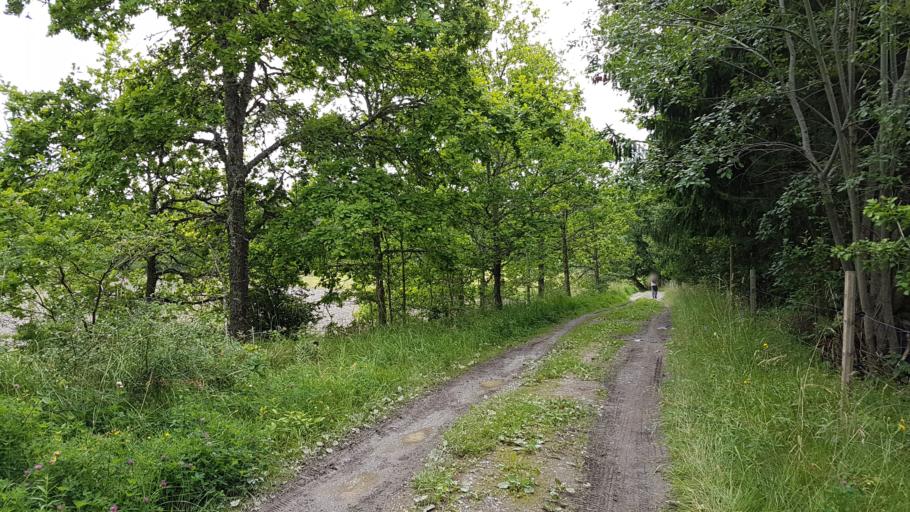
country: SE
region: OEstergoetland
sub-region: Valdemarsviks Kommun
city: Gusum
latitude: 58.4306
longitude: 16.5705
